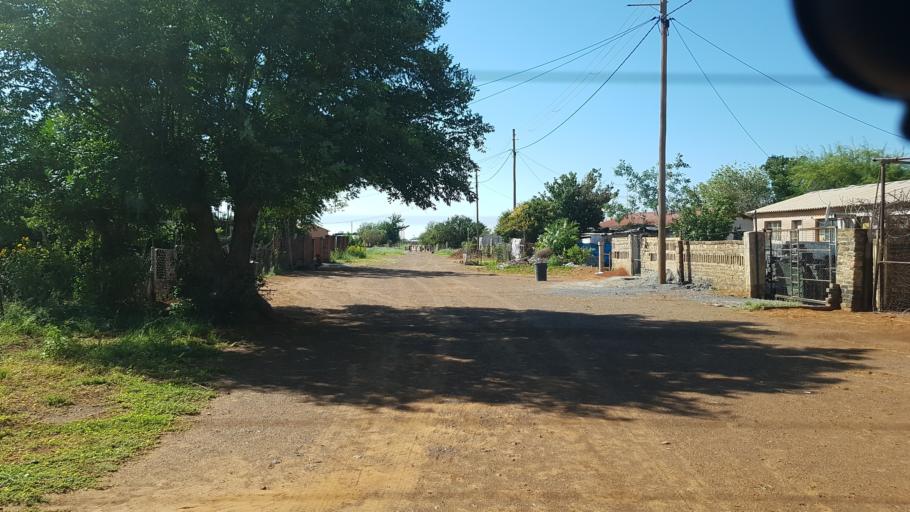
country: ZA
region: Northern Cape
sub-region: Siyanda District Municipality
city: Danielskuil
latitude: -28.1917
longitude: 23.5357
